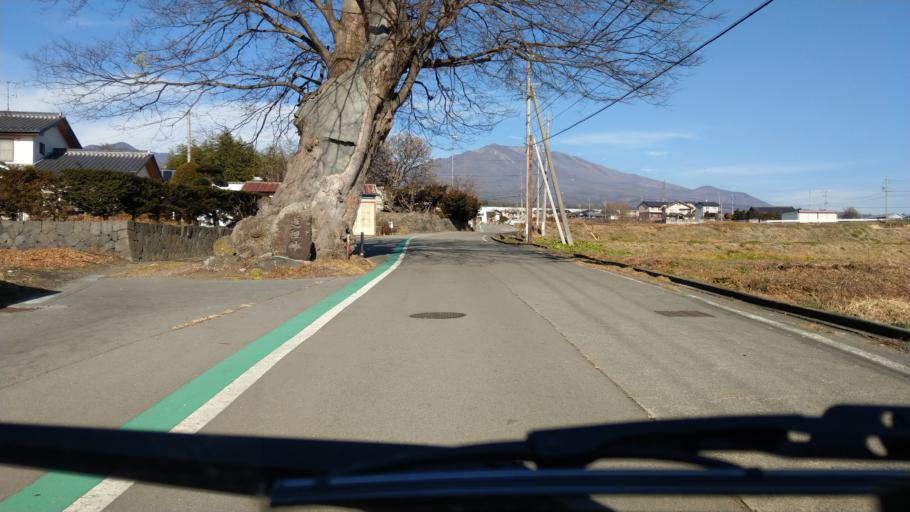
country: JP
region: Nagano
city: Komoro
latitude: 36.3237
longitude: 138.4550
